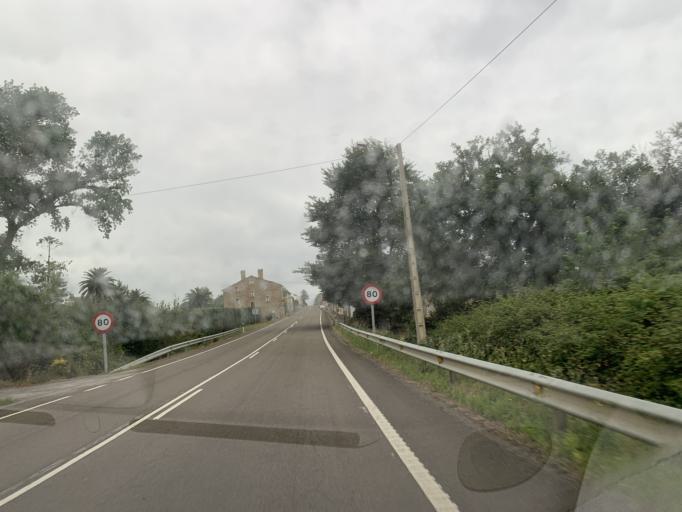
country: ES
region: Galicia
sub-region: Provincia de Lugo
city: Ribadeo
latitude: 43.5472
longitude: -7.1215
